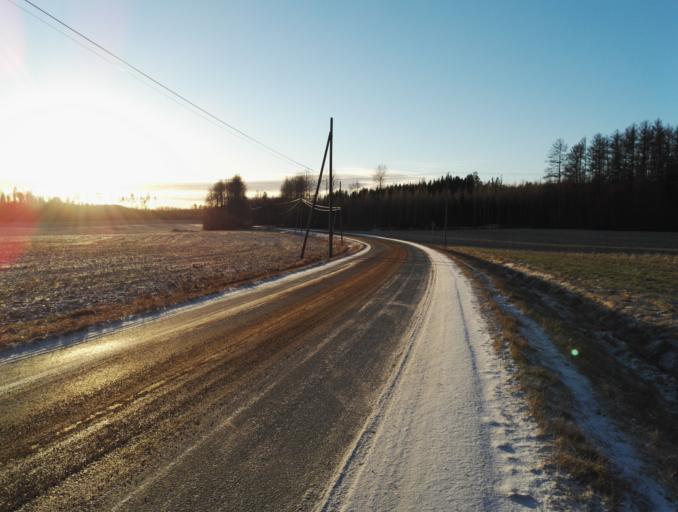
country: FI
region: Haeme
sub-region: Haemeenlinna
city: Janakkala
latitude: 60.8860
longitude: 24.5889
